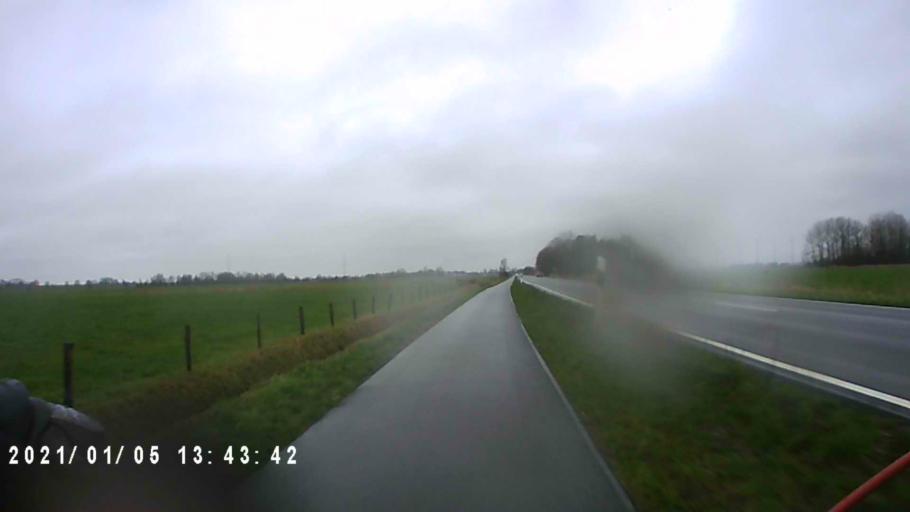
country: DE
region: Lower Saxony
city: Weener
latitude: 53.1948
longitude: 7.3957
